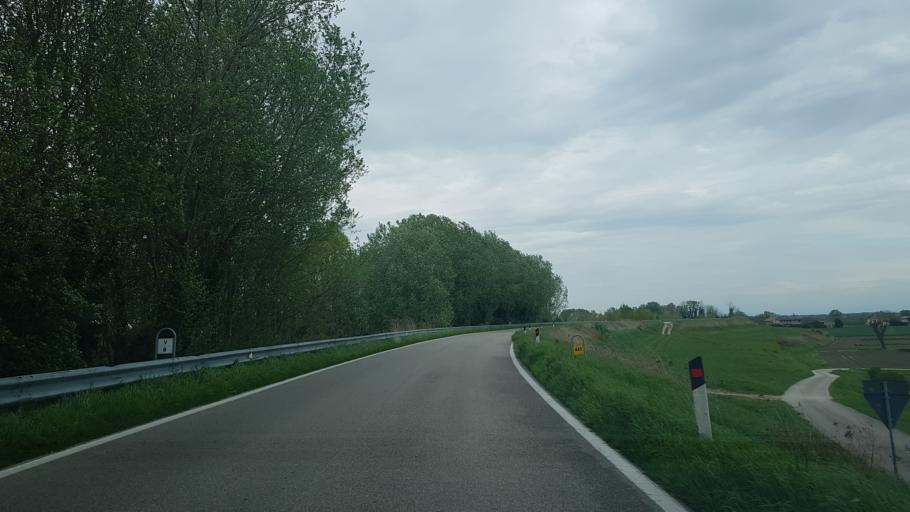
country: IT
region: Veneto
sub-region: Provincia di Padova
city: Barbona
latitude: 45.0983
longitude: 11.7226
